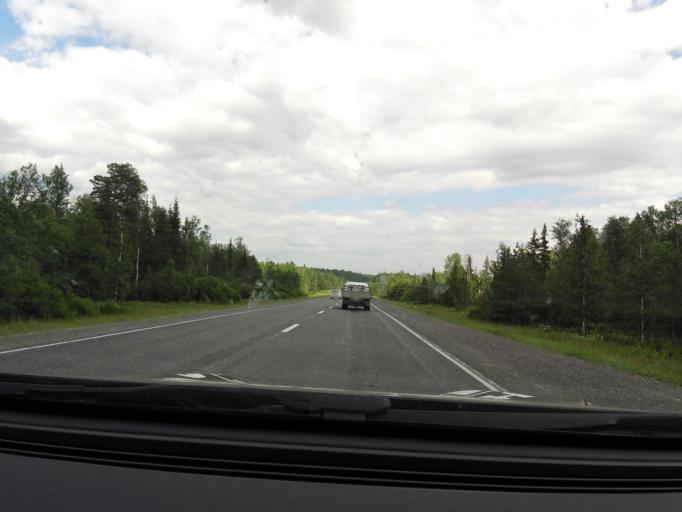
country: RU
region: Sverdlovsk
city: Nizhniye Sergi
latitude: 56.8249
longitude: 59.2555
